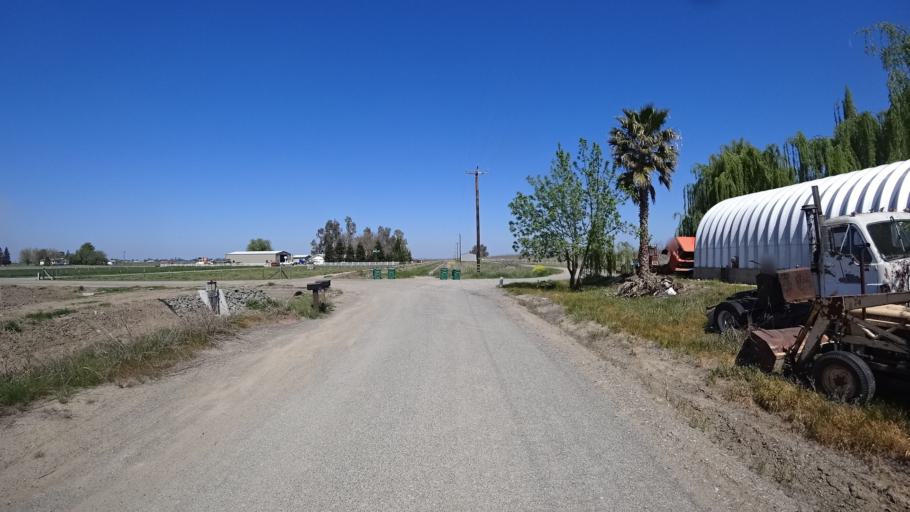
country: US
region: California
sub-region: Glenn County
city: Hamilton City
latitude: 39.5651
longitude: -122.0186
